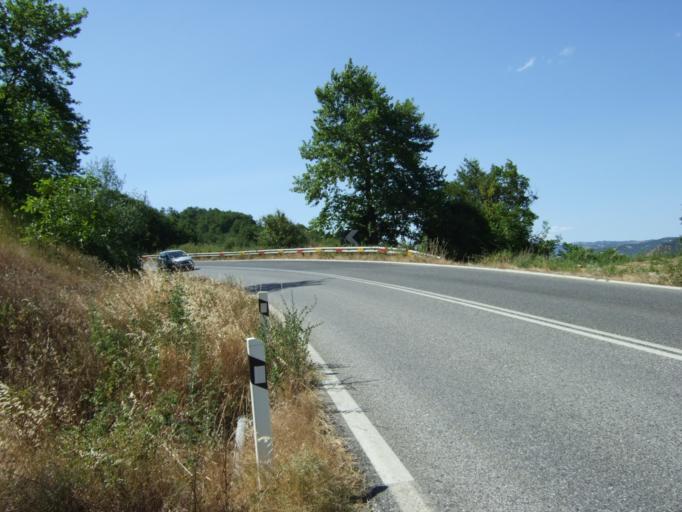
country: GR
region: Thessaly
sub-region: Trikala
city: Kastraki
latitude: 39.7418
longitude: 21.5384
